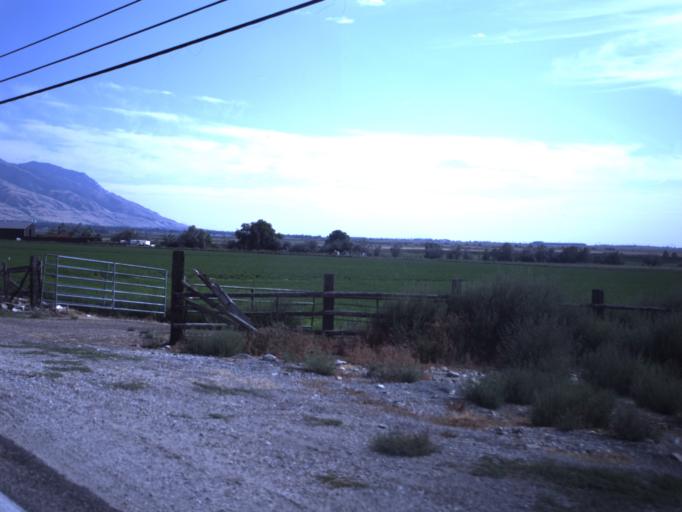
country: US
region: Utah
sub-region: Box Elder County
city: Honeyville
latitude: 41.5817
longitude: -112.0368
